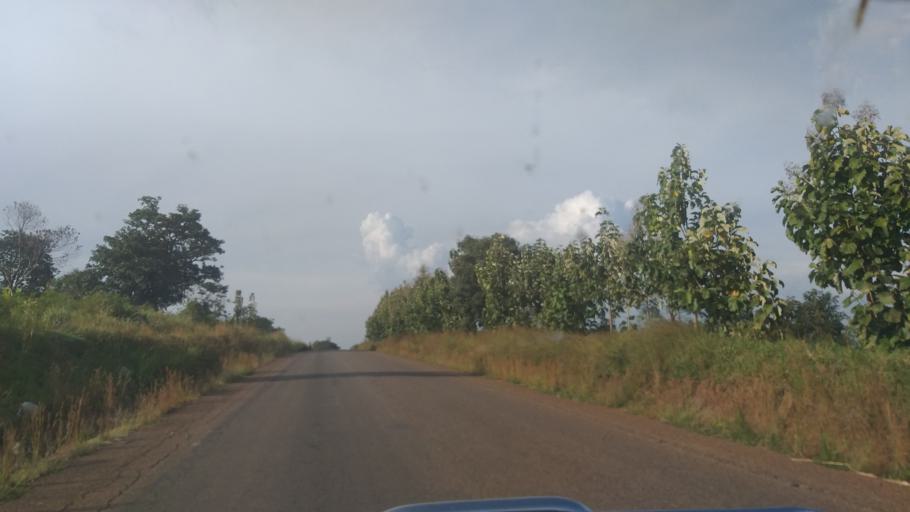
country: UG
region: Northern Region
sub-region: Arua District
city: Arua
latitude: 2.8366
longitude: 30.9930
